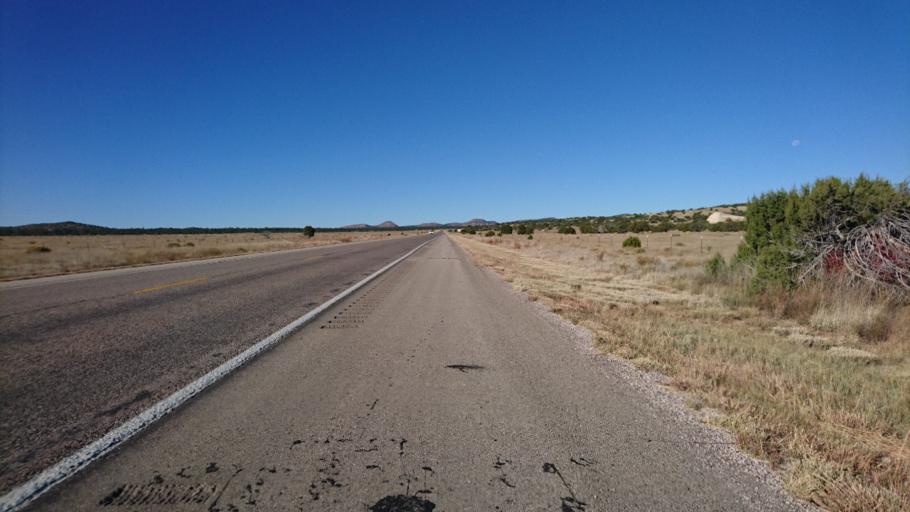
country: US
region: New Mexico
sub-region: Cibola County
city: Grants
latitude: 34.9604
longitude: -107.9205
